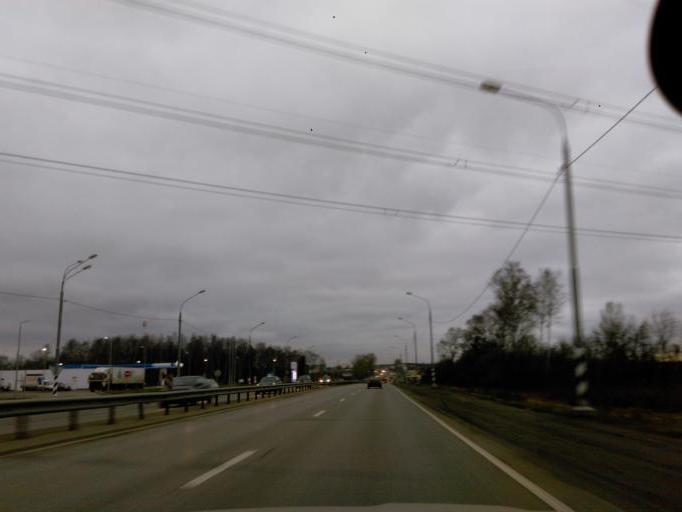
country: RU
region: Moskovskaya
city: Chashnikovo
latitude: 56.0440
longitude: 37.1582
